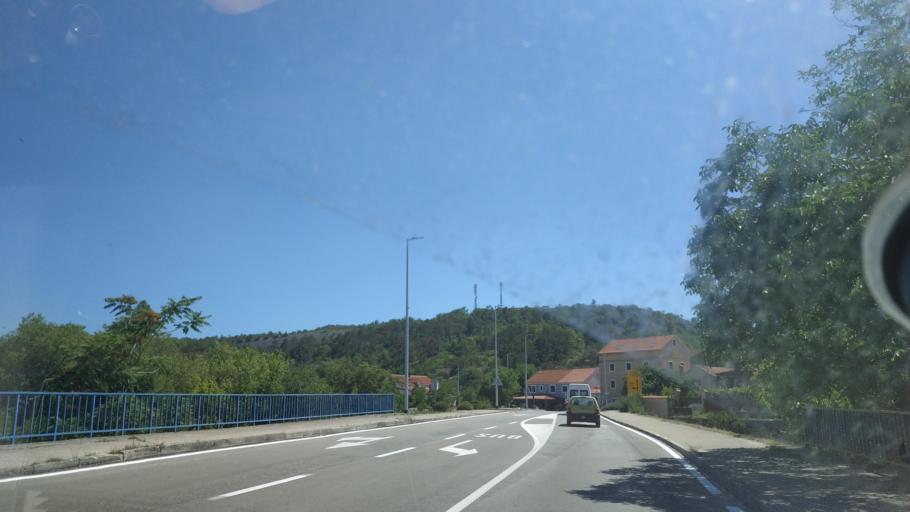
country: HR
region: Sibensko-Kniniska
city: Drnis
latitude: 43.8585
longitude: 16.1591
